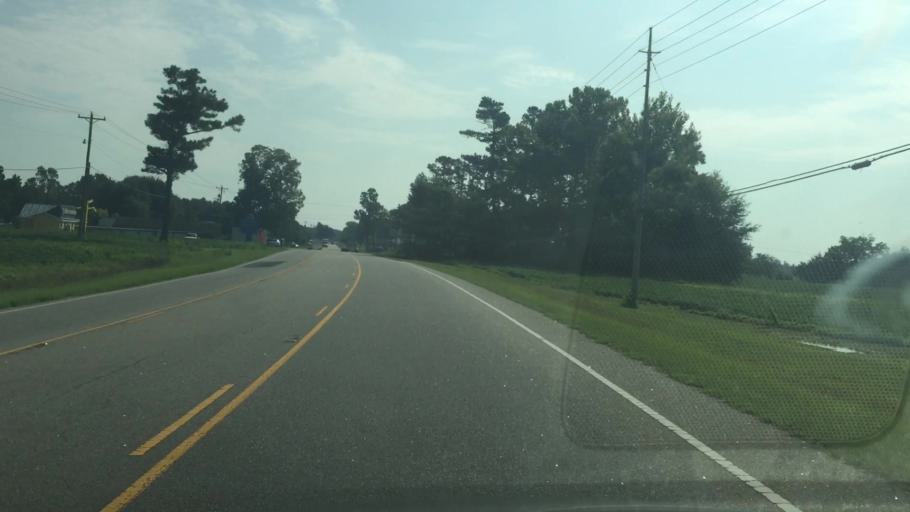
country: US
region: North Carolina
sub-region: Columbus County
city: Tabor City
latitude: 34.1596
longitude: -78.8496
